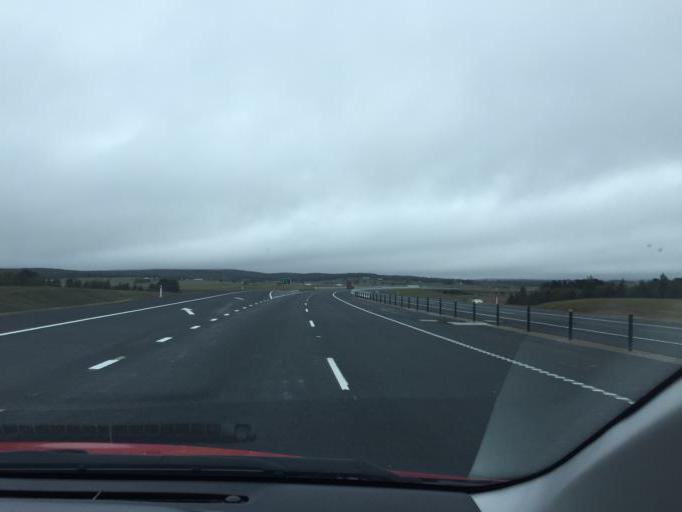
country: AU
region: Victoria
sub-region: Ballarat North
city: Newington
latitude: -37.4408
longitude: 143.4761
